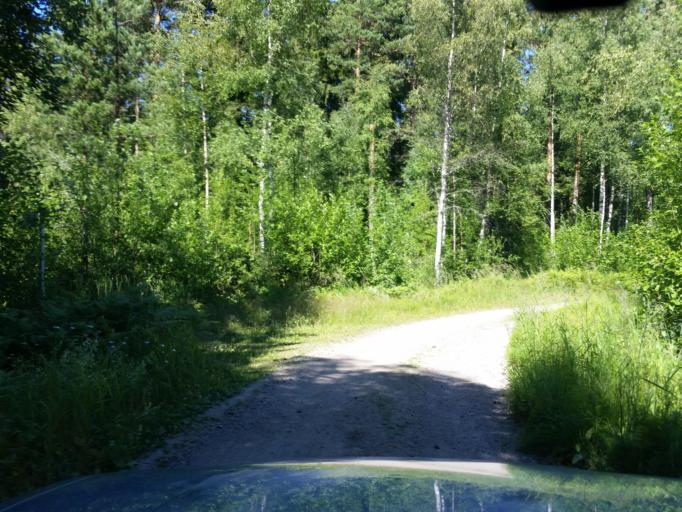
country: FI
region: Varsinais-Suomi
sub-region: Aboland-Turunmaa
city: Nagu
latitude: 60.2092
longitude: 22.0940
